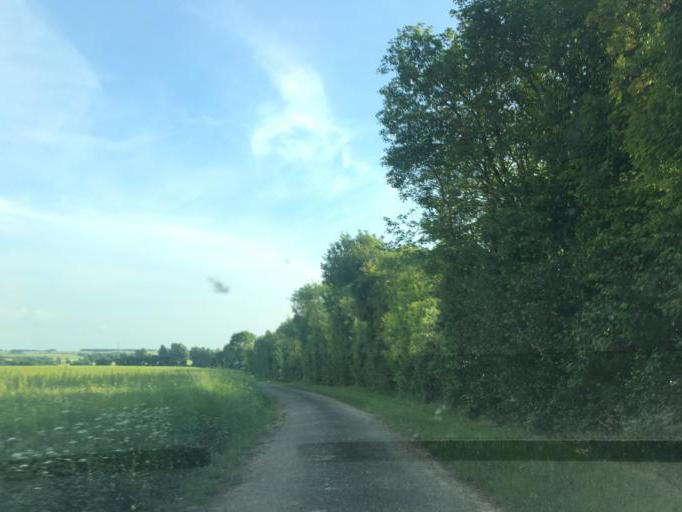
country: FR
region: Poitou-Charentes
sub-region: Departement de la Charente-Maritime
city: Saint-Jean-d'Angely
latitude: 46.0777
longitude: -0.5727
